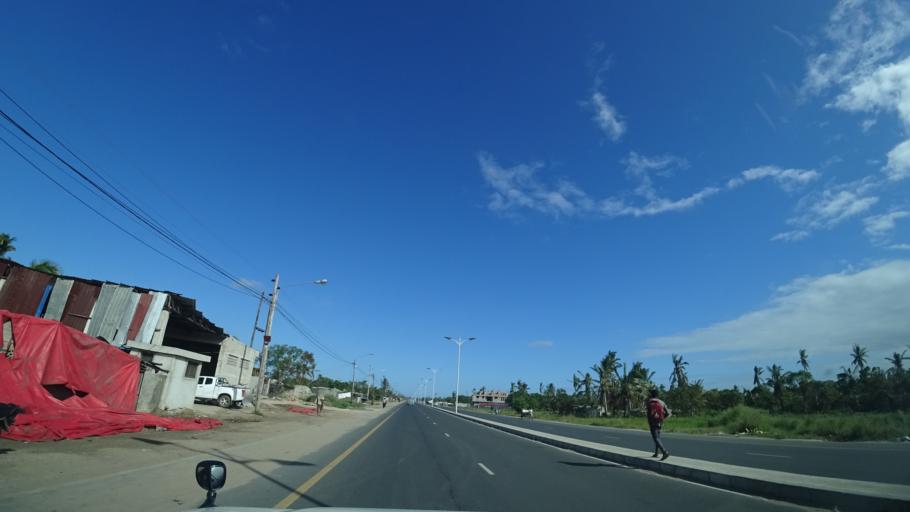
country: MZ
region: Sofala
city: Beira
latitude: -19.7378
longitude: 34.8451
